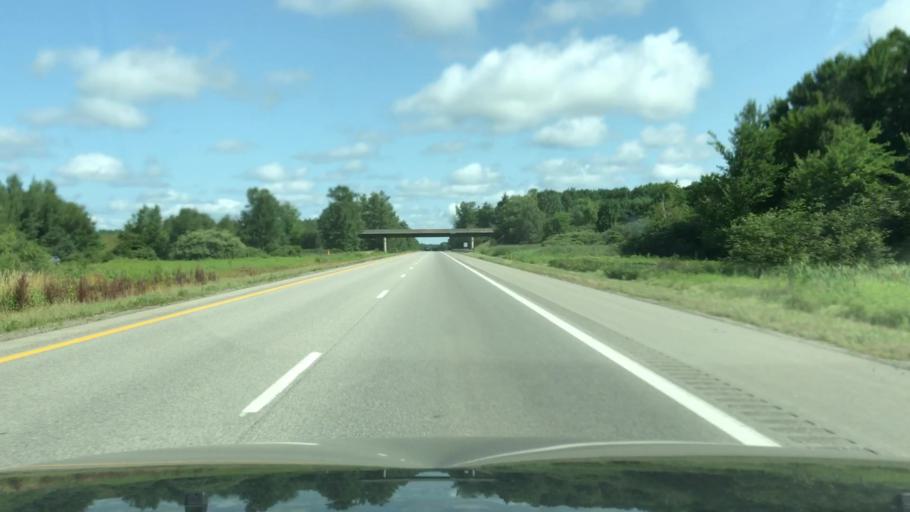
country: US
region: Michigan
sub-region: Montcalm County
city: Howard City
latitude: 43.5232
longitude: -85.4860
